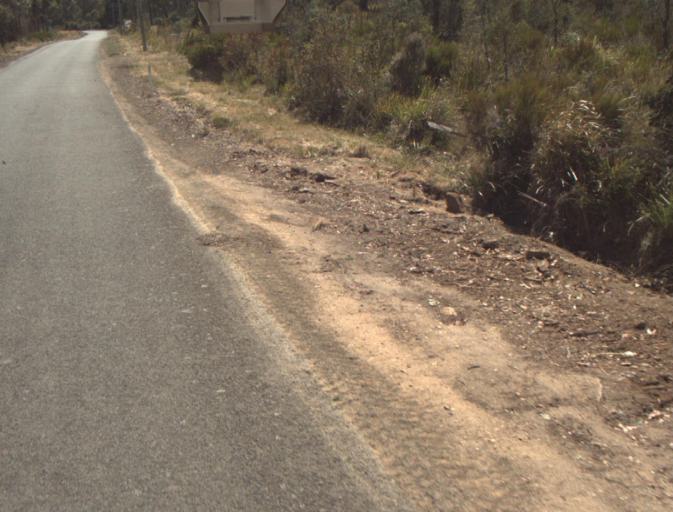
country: AU
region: Tasmania
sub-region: Launceston
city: Newstead
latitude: -41.3856
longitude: 147.2968
